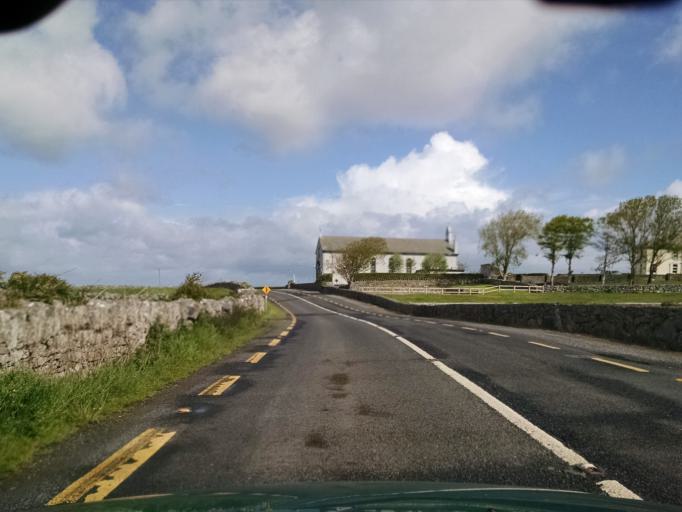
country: IE
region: Connaught
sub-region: County Galway
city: Gaillimh
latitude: 53.1354
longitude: -9.0667
